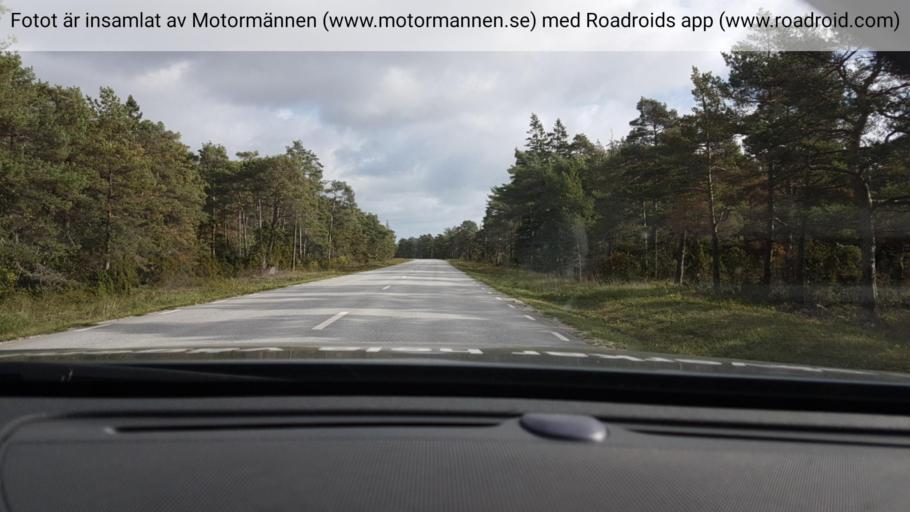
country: SE
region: Gotland
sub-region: Gotland
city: Slite
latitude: 57.7548
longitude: 18.7508
